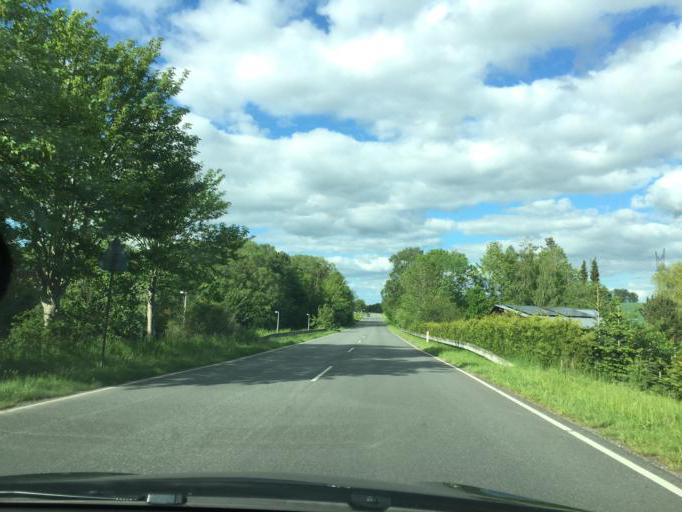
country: DK
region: South Denmark
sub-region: Odense Kommune
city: Bellinge
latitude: 55.3414
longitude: 10.3222
